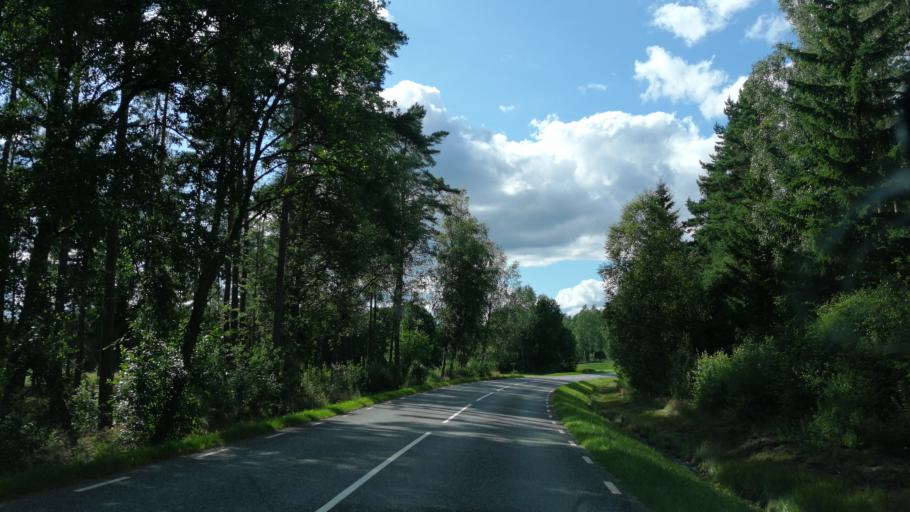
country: SE
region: Joenkoeping
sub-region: Gislaveds Kommun
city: Reftele
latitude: 57.1375
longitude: 13.6365
